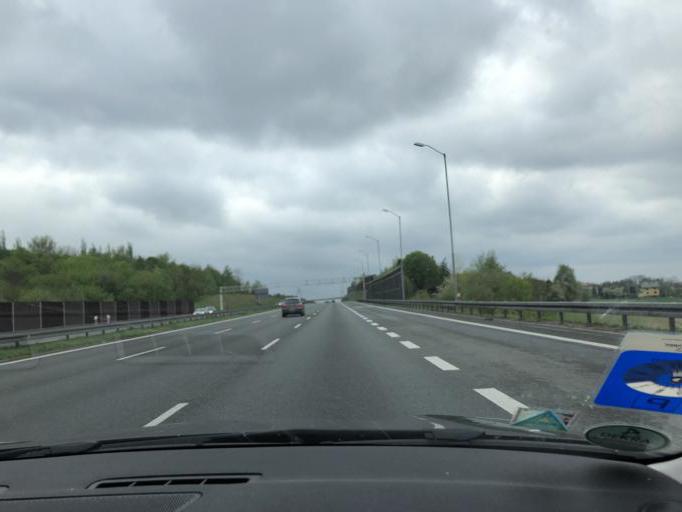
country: PL
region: Silesian Voivodeship
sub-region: Swietochlowice
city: Swietochlowice
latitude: 50.2525
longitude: 18.9275
